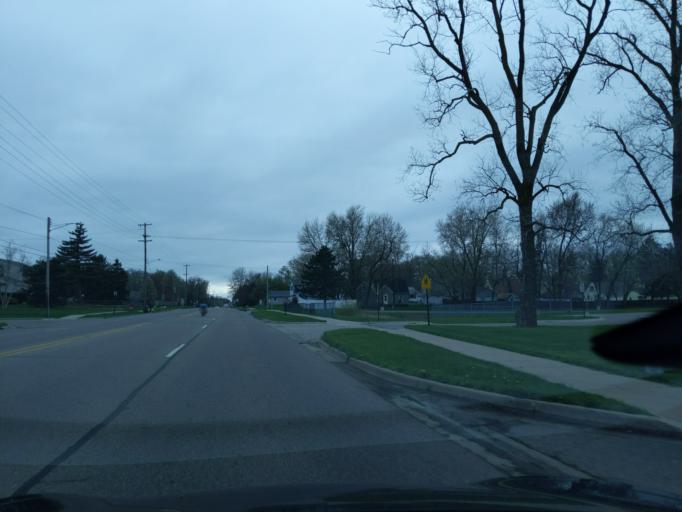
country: US
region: Michigan
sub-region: Eaton County
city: Waverly
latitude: 42.7339
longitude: -84.6114
